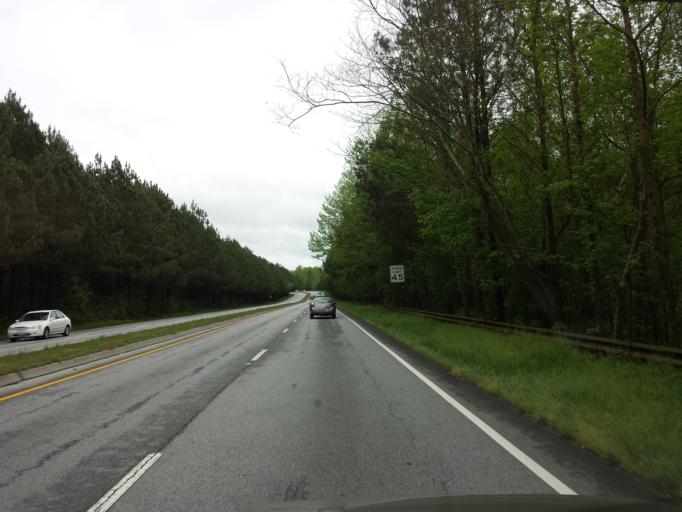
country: US
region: Georgia
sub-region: Cobb County
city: Mableton
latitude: 33.8480
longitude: -84.5514
